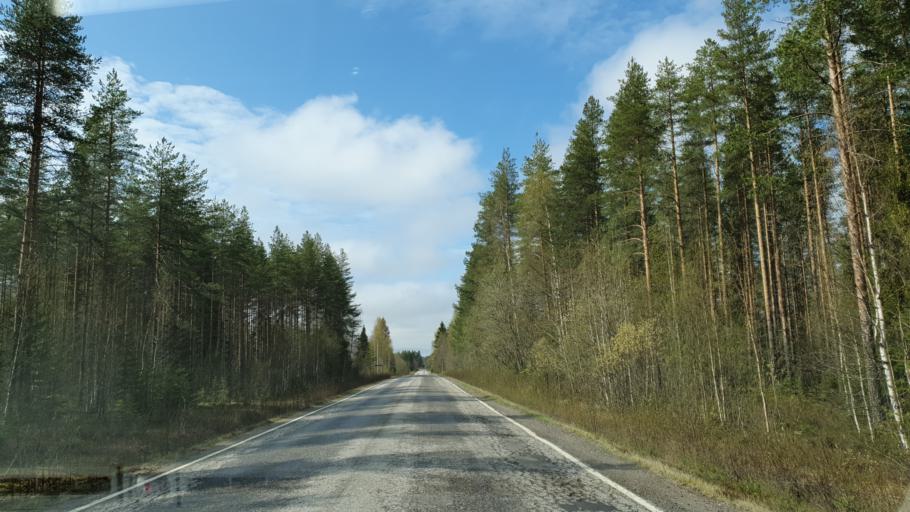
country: FI
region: Kainuu
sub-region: Kehys-Kainuu
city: Kuhmo
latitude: 64.1259
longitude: 29.6100
